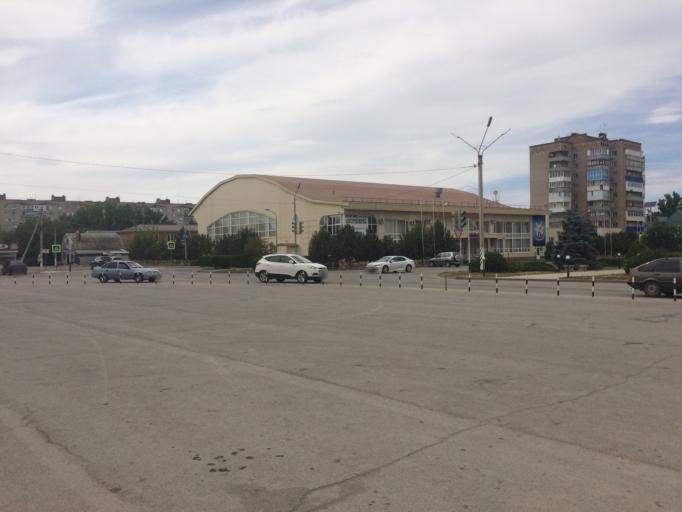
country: RU
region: Rostov
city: Sal'sk
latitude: 46.4785
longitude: 41.5383
